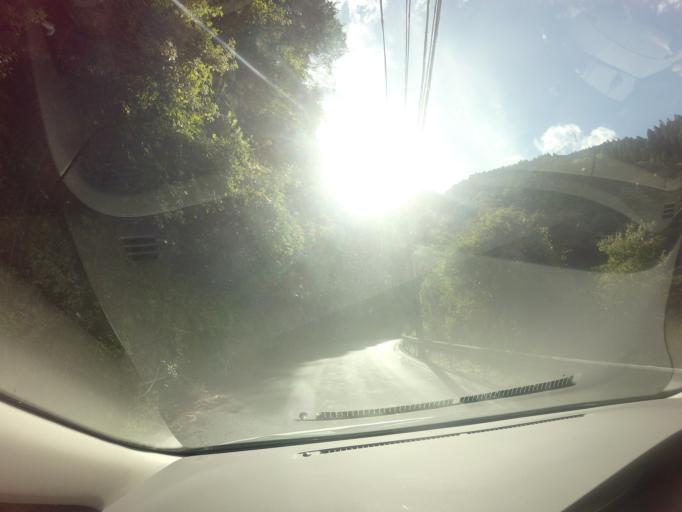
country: JP
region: Wakayama
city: Shingu
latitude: 33.9660
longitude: 135.8490
